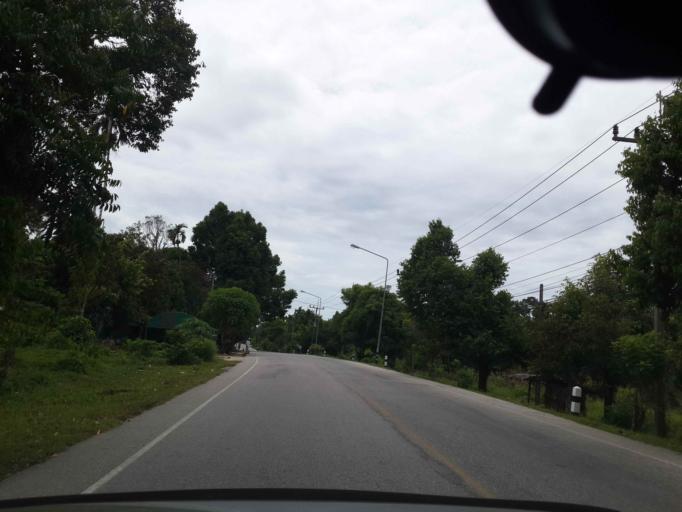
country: TH
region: Narathiwat
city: Yi-ngo
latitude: 6.3451
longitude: 101.6246
